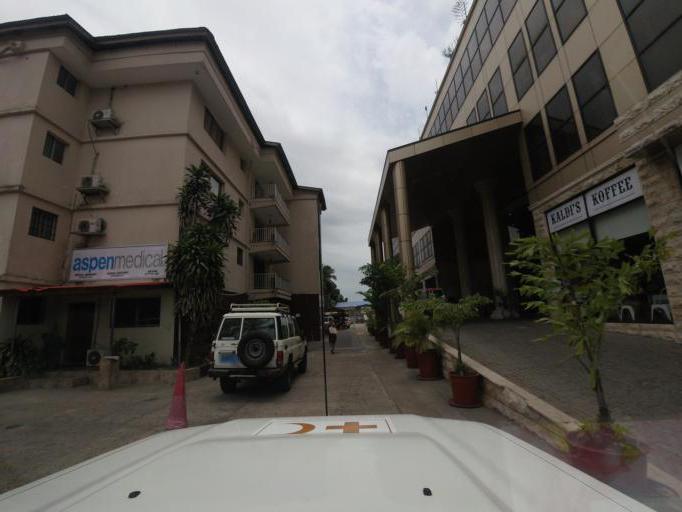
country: LR
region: Montserrado
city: Monrovia
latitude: 6.2920
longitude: -10.7794
